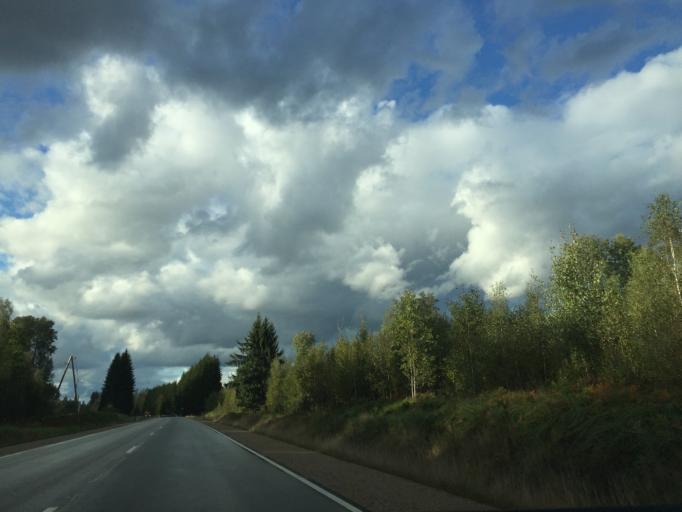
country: LV
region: Ligatne
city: Ligatne
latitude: 57.1505
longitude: 25.0729
